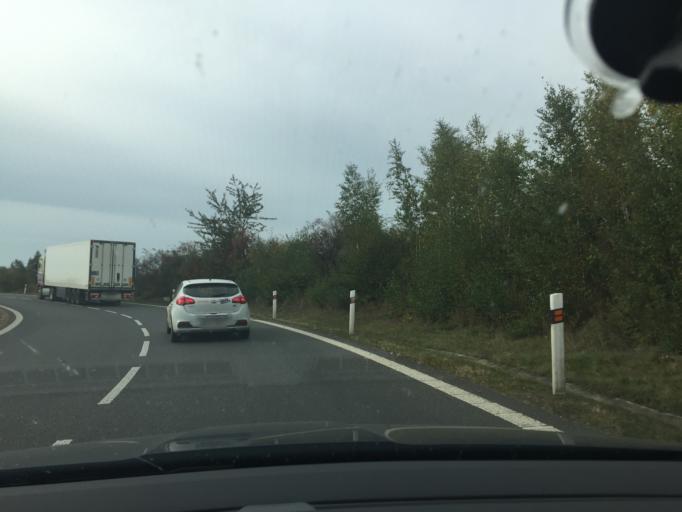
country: CZ
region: Central Bohemia
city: Jirny
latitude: 50.1235
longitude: 14.7062
